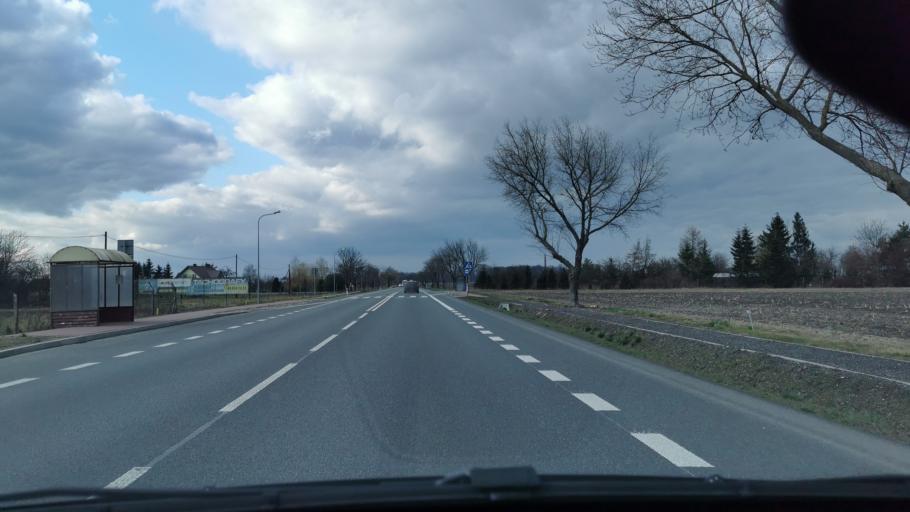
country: PL
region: Masovian Voivodeship
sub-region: Powiat zyrardowski
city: Guzow
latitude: 52.1050
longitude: 20.3463
